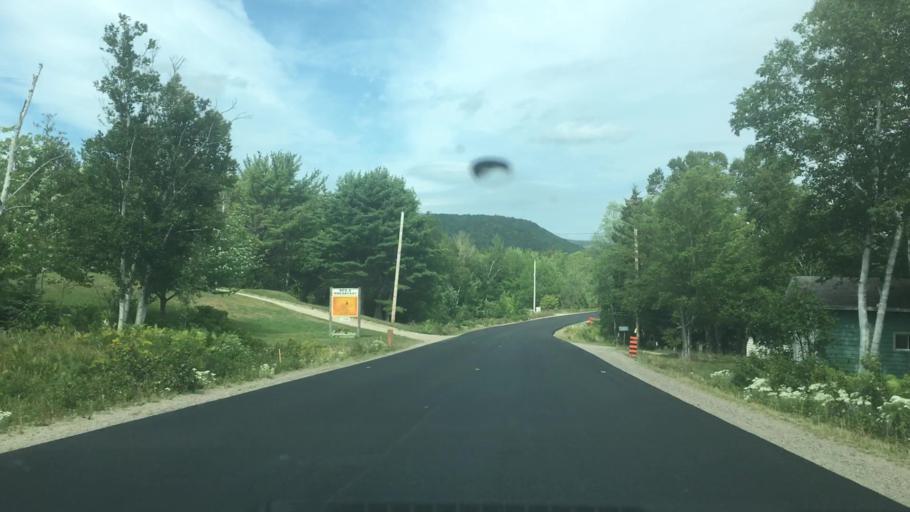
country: CA
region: Nova Scotia
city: Sydney Mines
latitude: 46.5489
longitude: -60.4120
